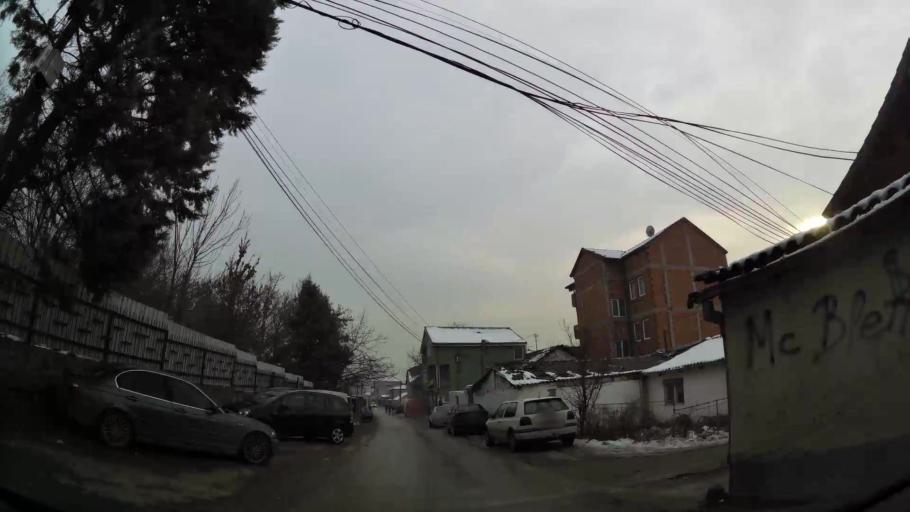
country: MK
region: Suto Orizari
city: Suto Orizare
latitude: 42.0322
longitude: 21.4335
